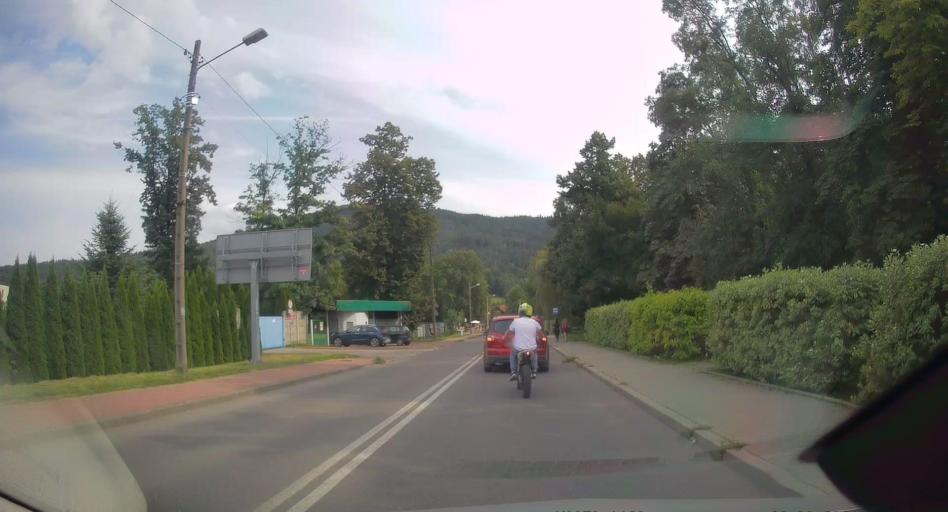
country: PL
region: Lesser Poland Voivodeship
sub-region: Powiat myslenicki
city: Myslenice
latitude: 49.8231
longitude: 19.9458
